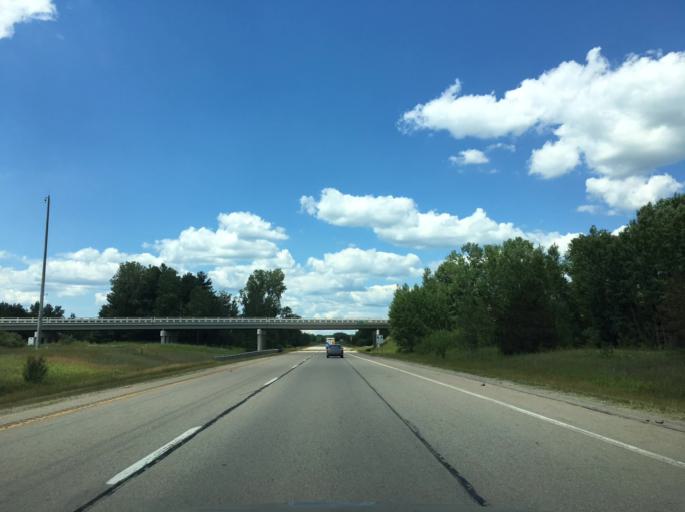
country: US
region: Michigan
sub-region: Clare County
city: Clare
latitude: 43.8811
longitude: -84.7863
